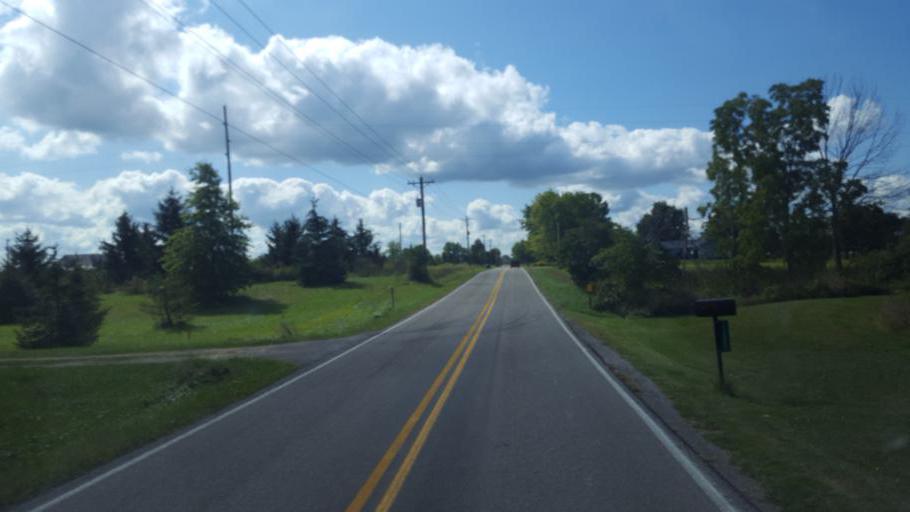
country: US
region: Ohio
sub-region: Lorain County
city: Lagrange
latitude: 41.1482
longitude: -82.0898
